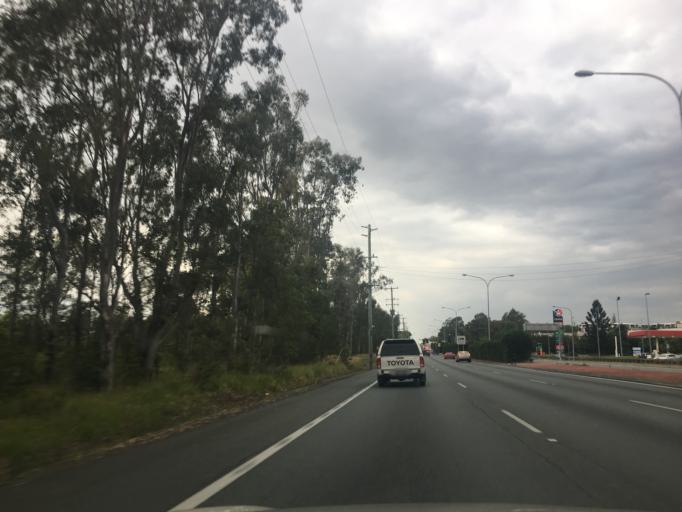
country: AU
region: Queensland
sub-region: Brisbane
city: Bald Hills
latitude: -27.3410
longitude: 153.0110
